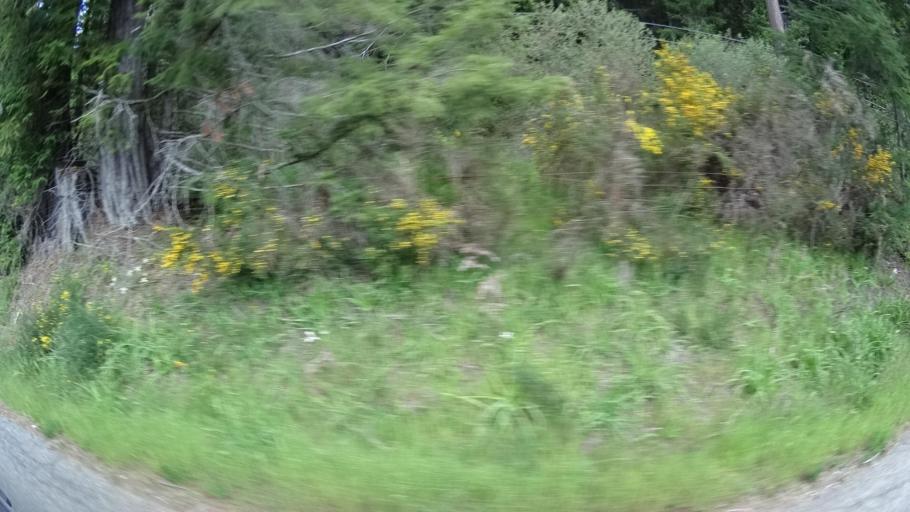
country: US
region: California
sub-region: Humboldt County
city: Redway
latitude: 40.0311
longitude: -123.9510
